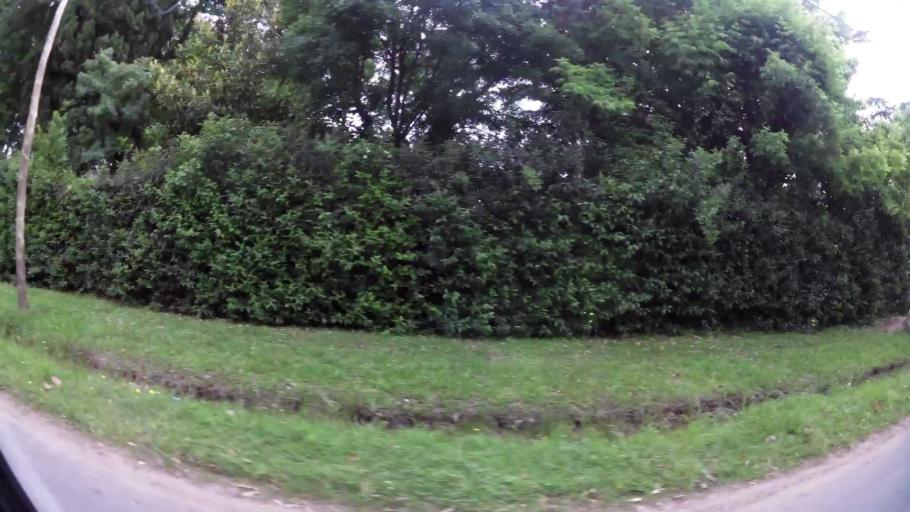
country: AR
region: Buenos Aires
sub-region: Partido de Ezeiza
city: Ezeiza
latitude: -34.8703
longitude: -58.5049
